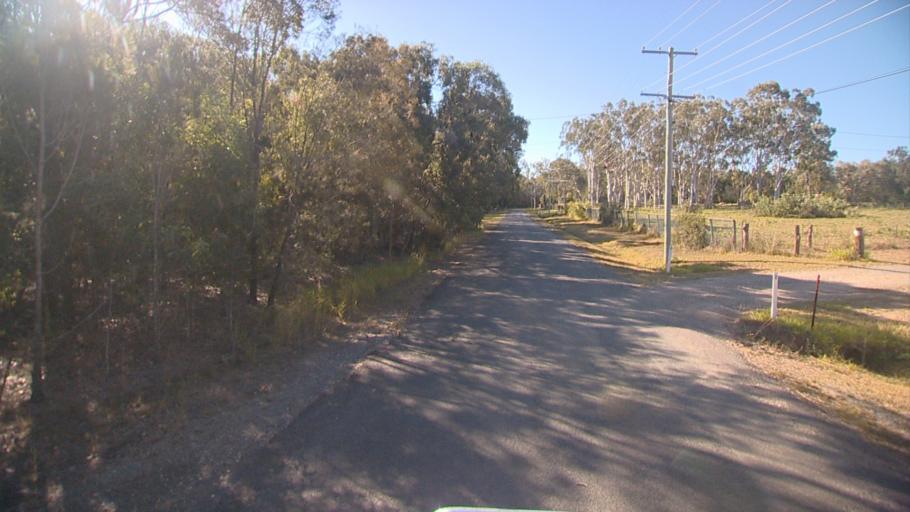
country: AU
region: Queensland
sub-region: Logan
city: Logan Reserve
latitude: -27.7308
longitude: 153.0830
